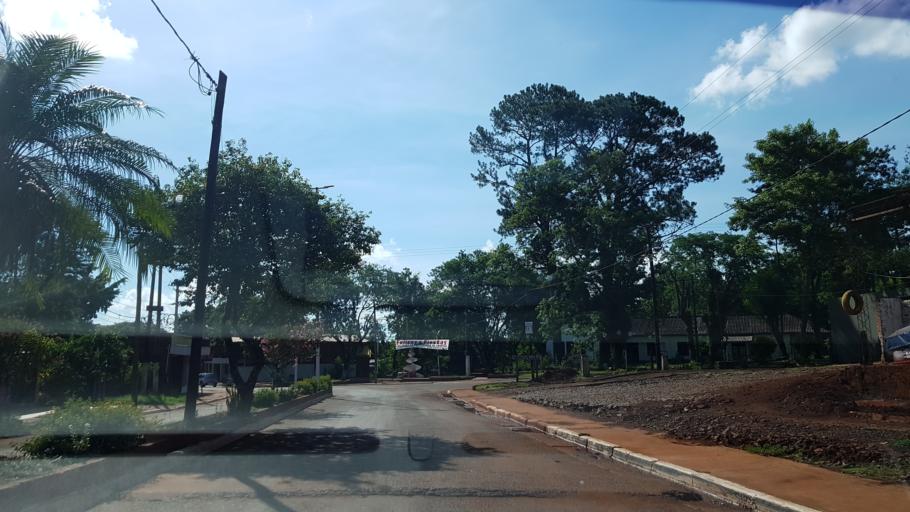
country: AR
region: Misiones
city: Puerto Libertad
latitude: -25.9209
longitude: -54.5786
